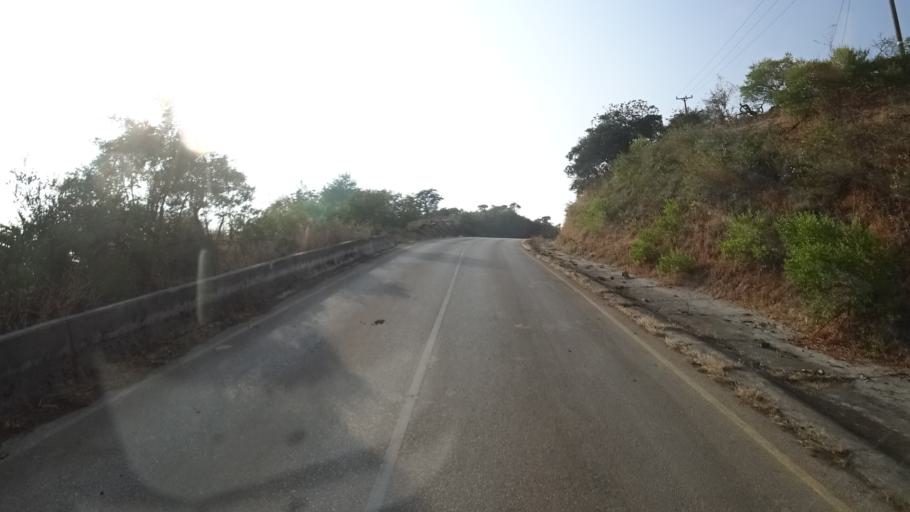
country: YE
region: Al Mahrah
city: Hawf
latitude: 16.7422
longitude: 53.3629
